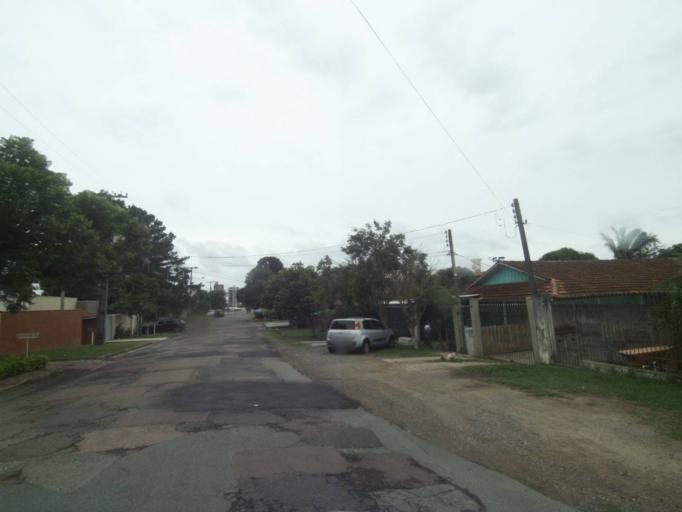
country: BR
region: Parana
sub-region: Curitiba
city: Curitiba
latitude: -25.4275
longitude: -49.3292
